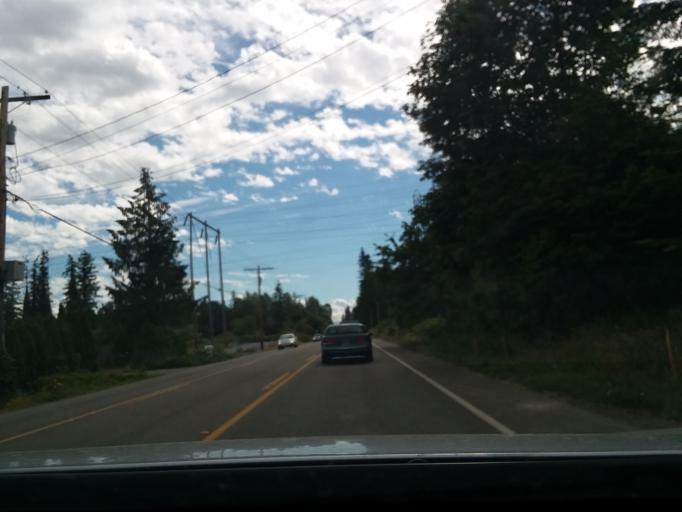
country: US
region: Washington
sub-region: Snohomish County
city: West Lake Stevens
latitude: 47.9781
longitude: -122.1152
